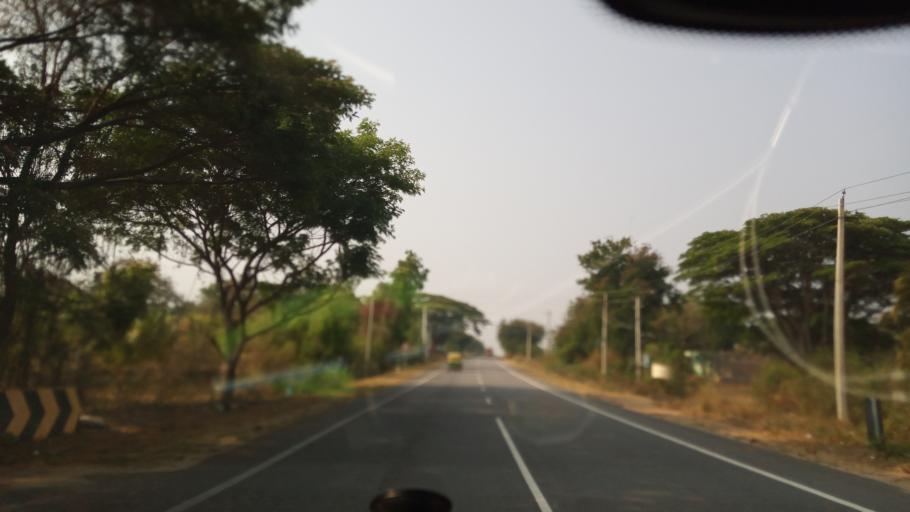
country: IN
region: Karnataka
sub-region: Mandya
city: Belluru
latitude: 12.9285
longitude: 76.7493
